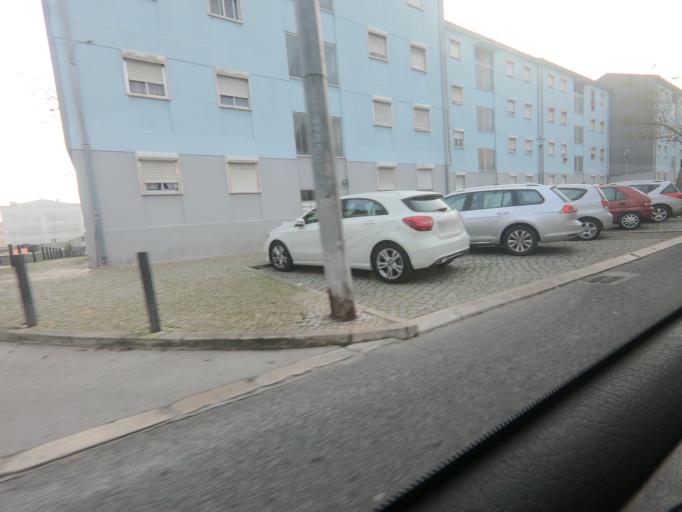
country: PT
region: Setubal
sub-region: Setubal
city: Setubal
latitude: 38.5265
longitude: -8.8751
